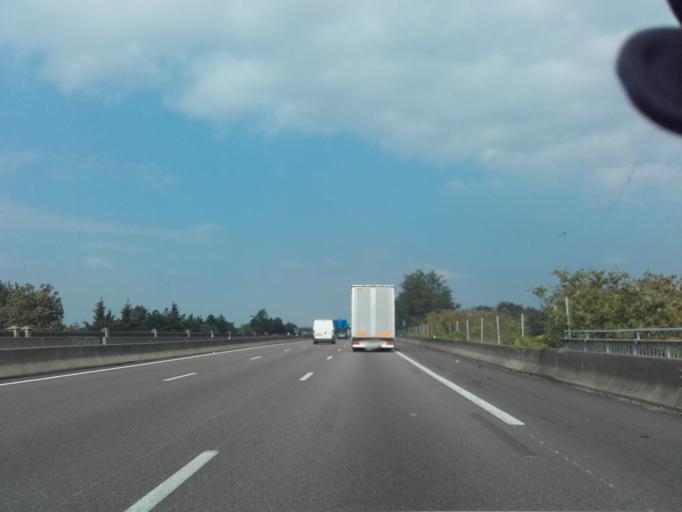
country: FR
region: Bourgogne
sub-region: Departement de Saone-et-Loire
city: Chatenoy-le-Royal
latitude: 46.7969
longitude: 4.8236
